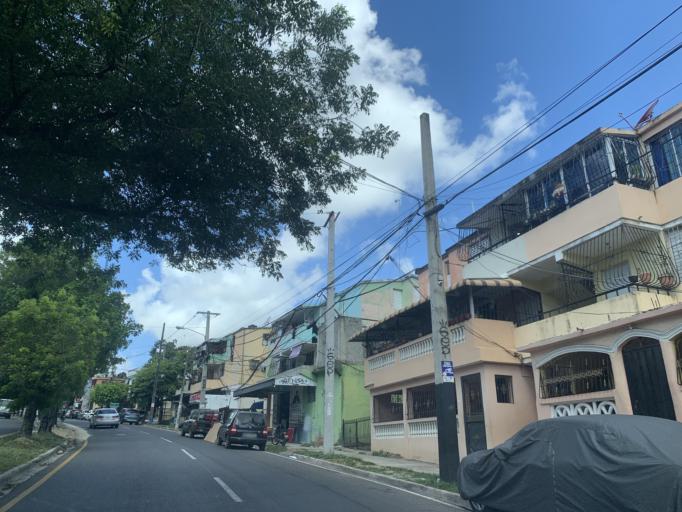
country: DO
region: Nacional
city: La Agustina
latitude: 18.5073
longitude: -69.9204
